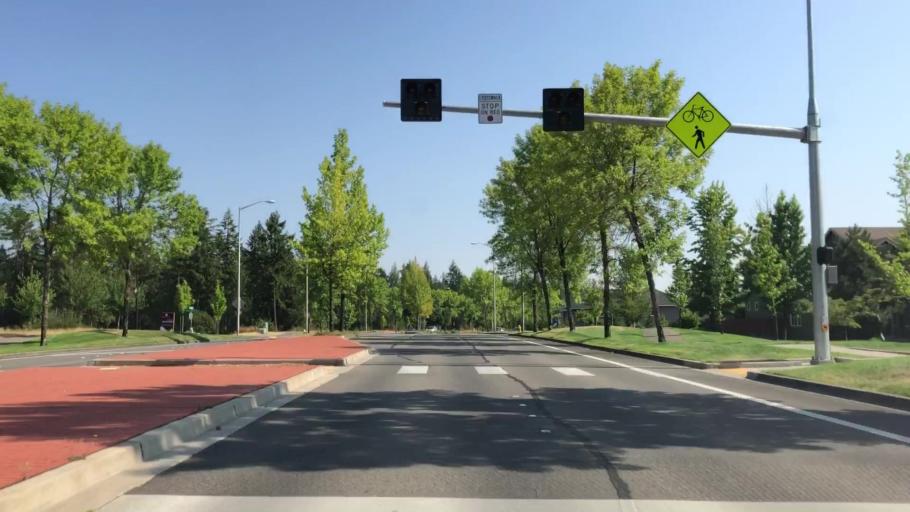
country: US
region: Washington
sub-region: Thurston County
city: Tanglewilde-Thompson Place
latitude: 47.0841
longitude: -122.7545
